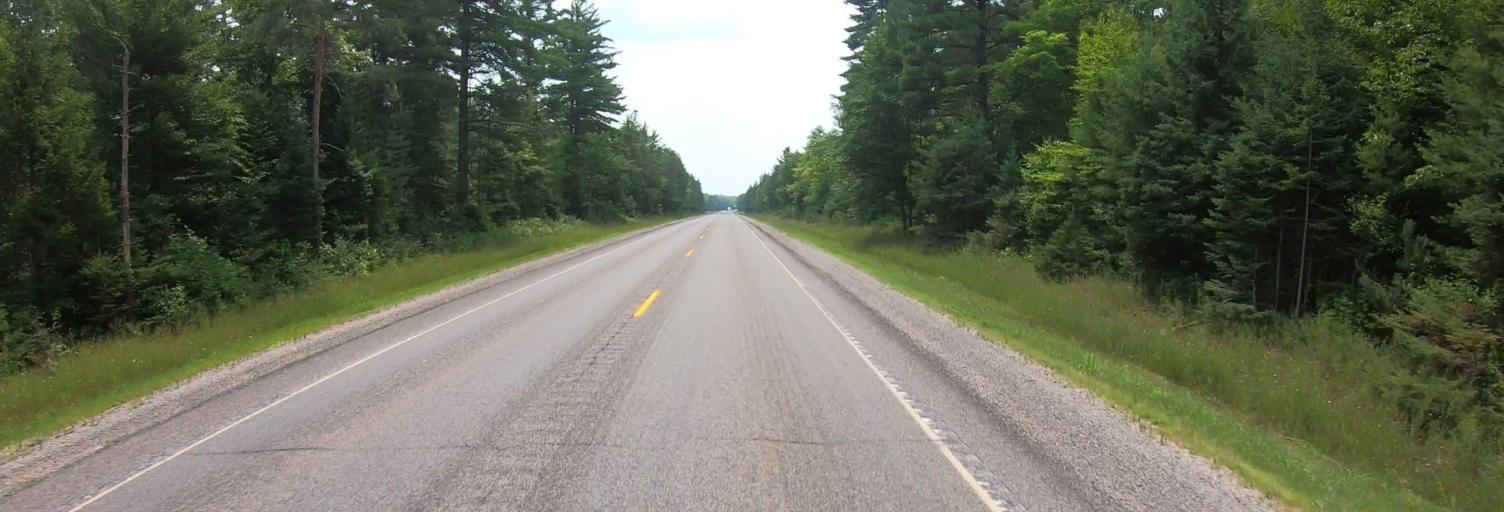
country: US
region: Michigan
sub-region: Alger County
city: Munising
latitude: 46.3453
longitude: -86.7289
